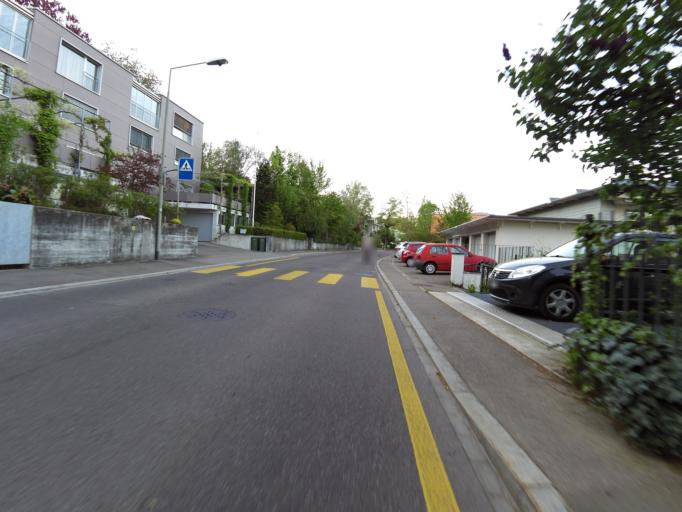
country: CH
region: Zurich
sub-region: Bezirk Winterthur
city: Oberwinterthur (Kreis 2) / Talacker
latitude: 47.5034
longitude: 8.7467
